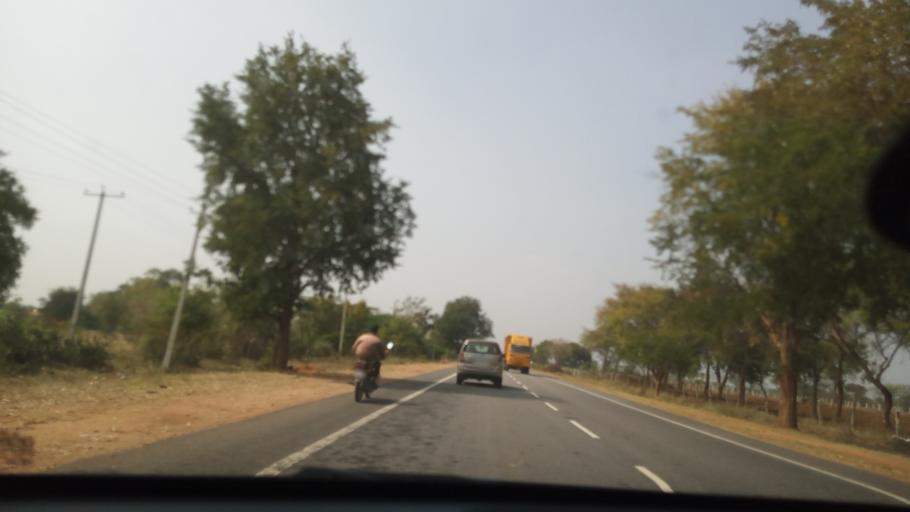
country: IN
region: Karnataka
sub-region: Mysore
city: Nanjangud
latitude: 12.0718
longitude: 76.7440
